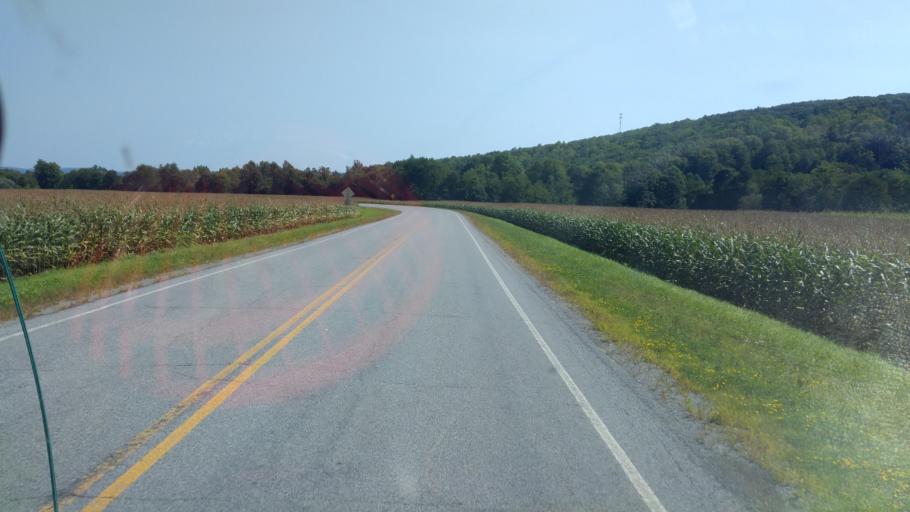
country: US
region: New York
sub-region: Allegany County
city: Belmont
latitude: 42.2381
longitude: -78.0799
